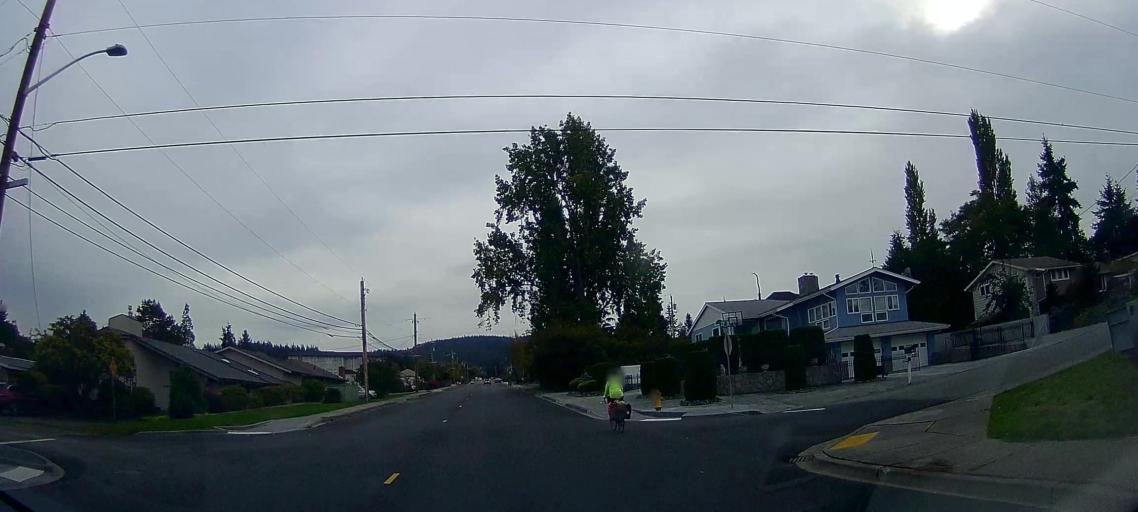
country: US
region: Washington
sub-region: Skagit County
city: Anacortes
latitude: 48.4958
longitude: -122.6176
